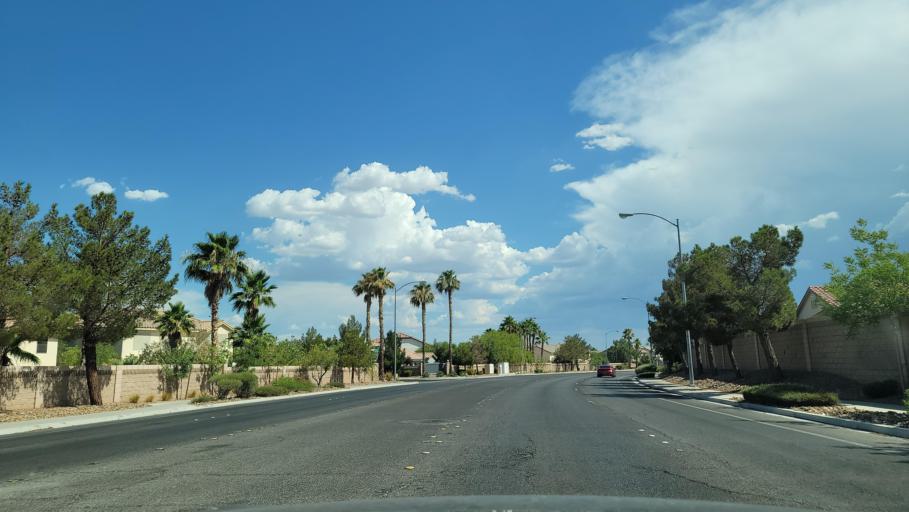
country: US
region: Nevada
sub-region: Clark County
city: Spring Valley
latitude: 36.1342
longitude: -115.2693
